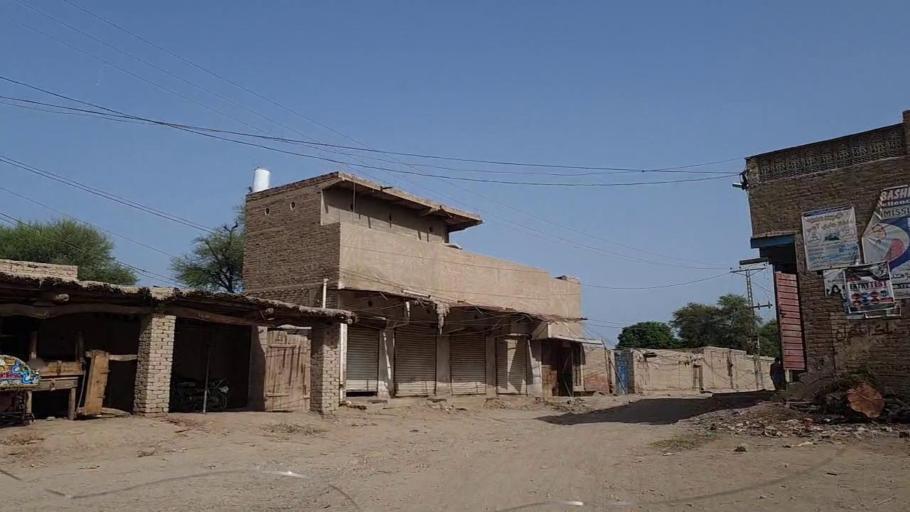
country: PK
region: Sindh
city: Kandiaro
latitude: 27.0650
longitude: 68.2061
